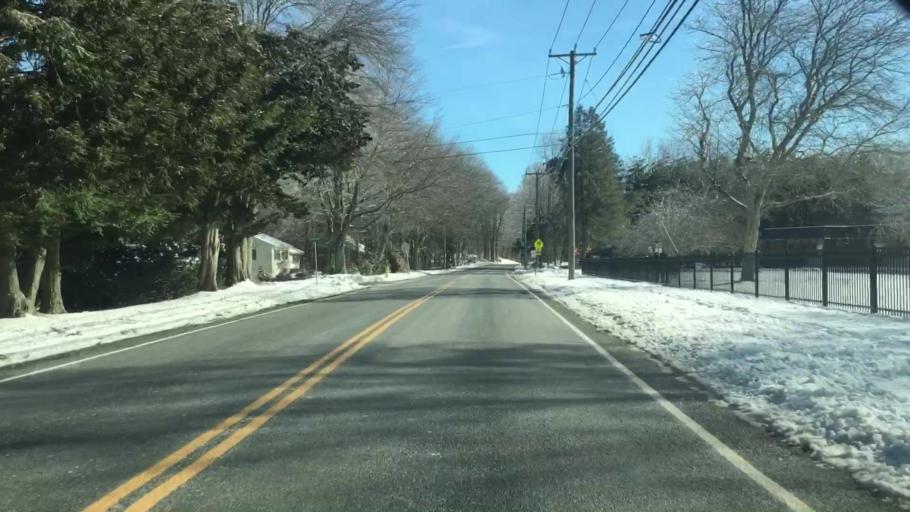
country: US
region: Connecticut
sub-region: Fairfield County
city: Newtown
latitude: 41.3460
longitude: -73.2299
